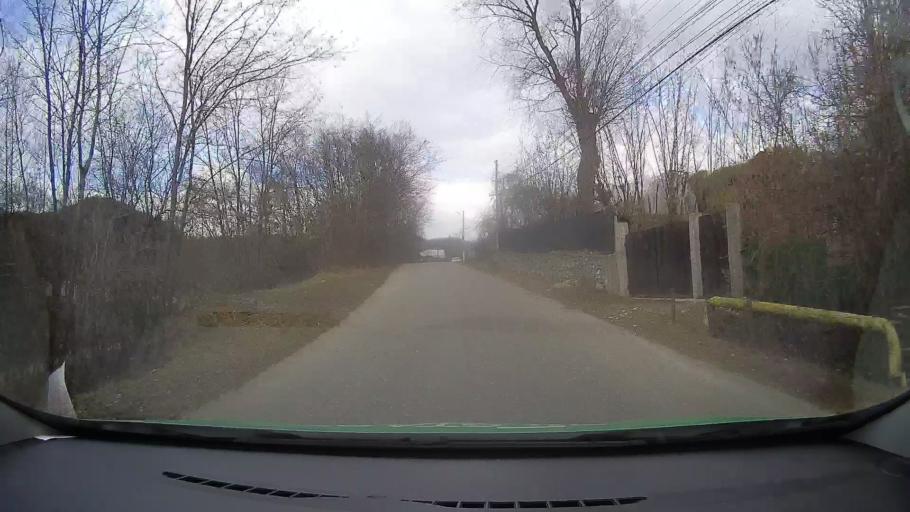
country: RO
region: Dambovita
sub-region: Comuna Visinesti
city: Visinesti
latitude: 45.1025
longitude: 25.5635
